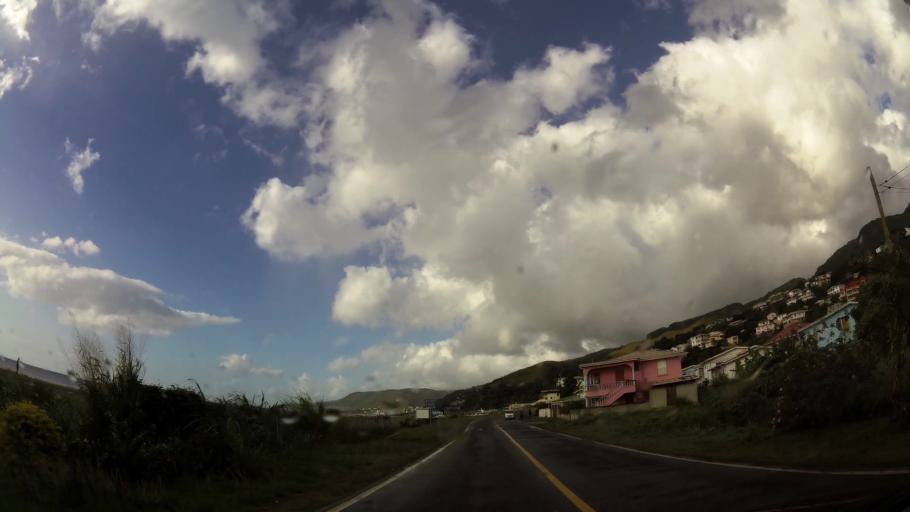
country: DM
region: Saint Paul
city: Mahaut
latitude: 15.3369
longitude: -61.3917
